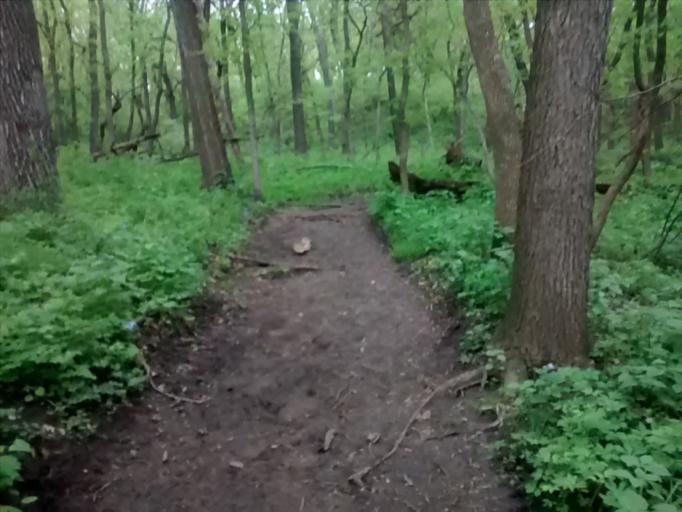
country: US
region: Nebraska
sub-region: Sarpy County
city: Bellevue
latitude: 41.1790
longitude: -95.9105
